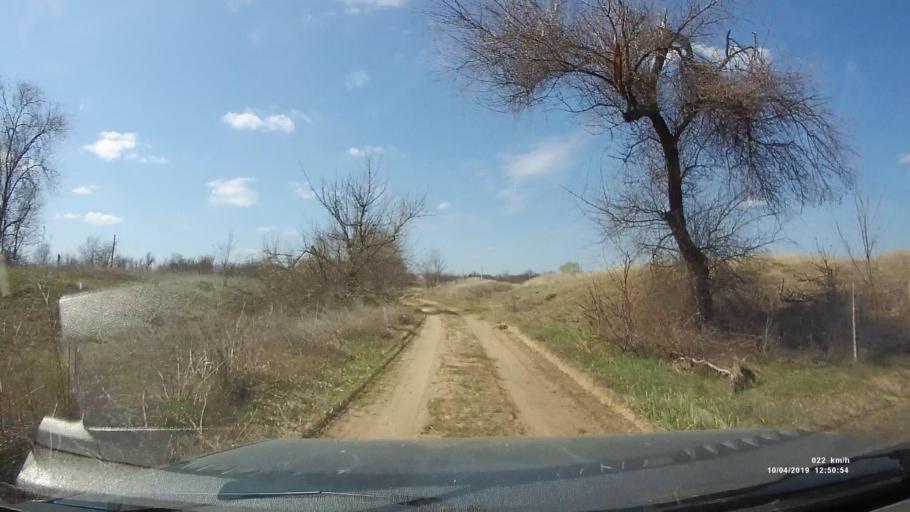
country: RU
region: Rostov
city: Kamensk-Shakhtinskiy
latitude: 48.3587
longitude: 40.2197
